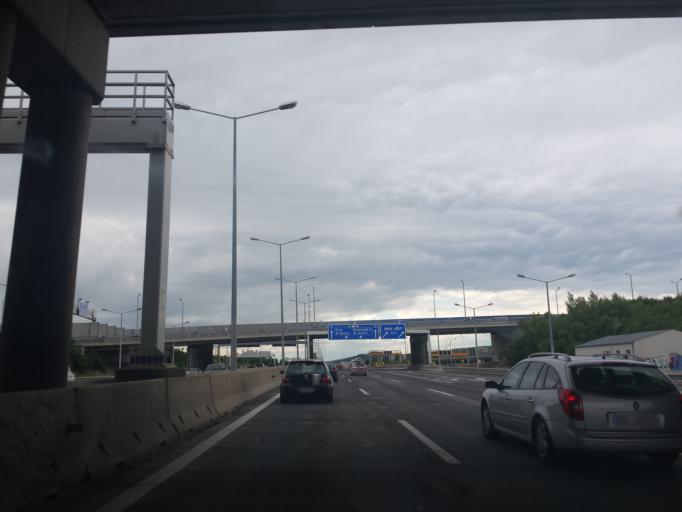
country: AT
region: Lower Austria
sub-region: Politischer Bezirk Modling
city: Vosendorf
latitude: 48.1204
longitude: 16.3247
